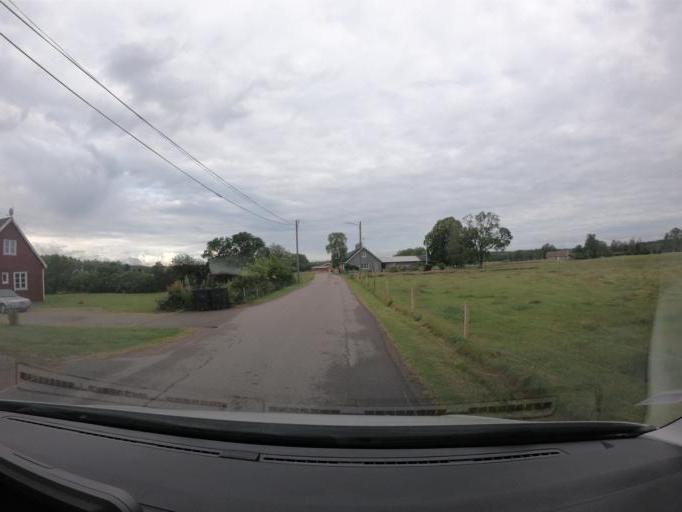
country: SE
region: Skane
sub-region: Klippans Kommun
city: Klippan
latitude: 56.2743
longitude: 13.1281
